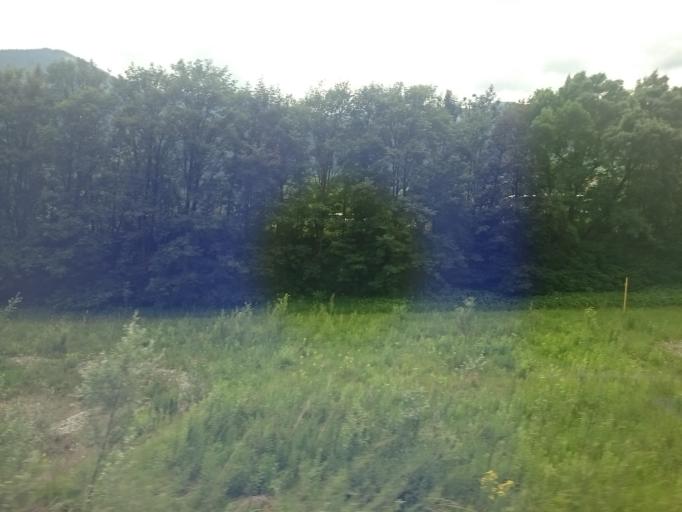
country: AT
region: Tyrol
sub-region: Politischer Bezirk Schwaz
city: Jenbach
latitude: 47.3860
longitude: 11.7626
